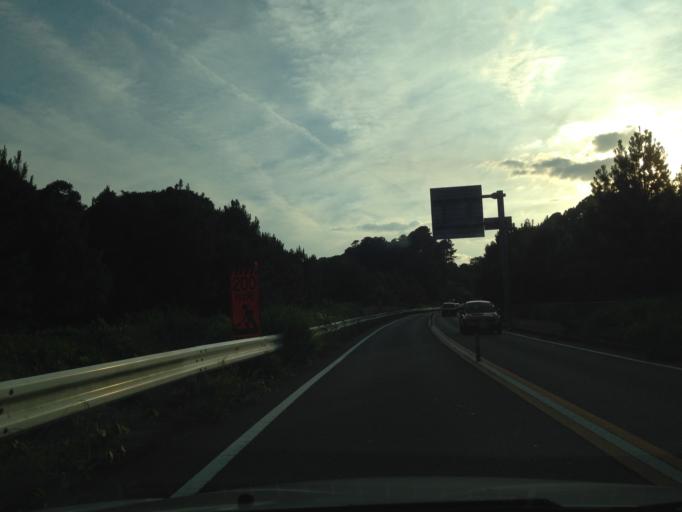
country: JP
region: Shizuoka
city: Kakegawa
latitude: 34.7522
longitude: 138.0083
